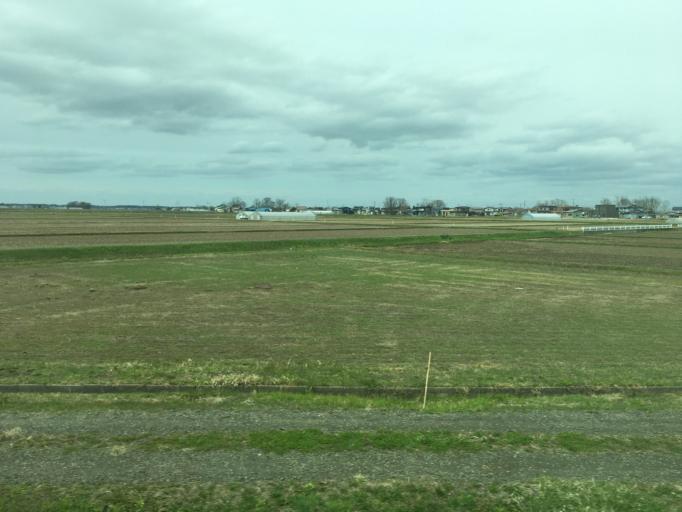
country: JP
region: Aomori
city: Shimokizukuri
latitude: 40.7850
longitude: 140.3603
